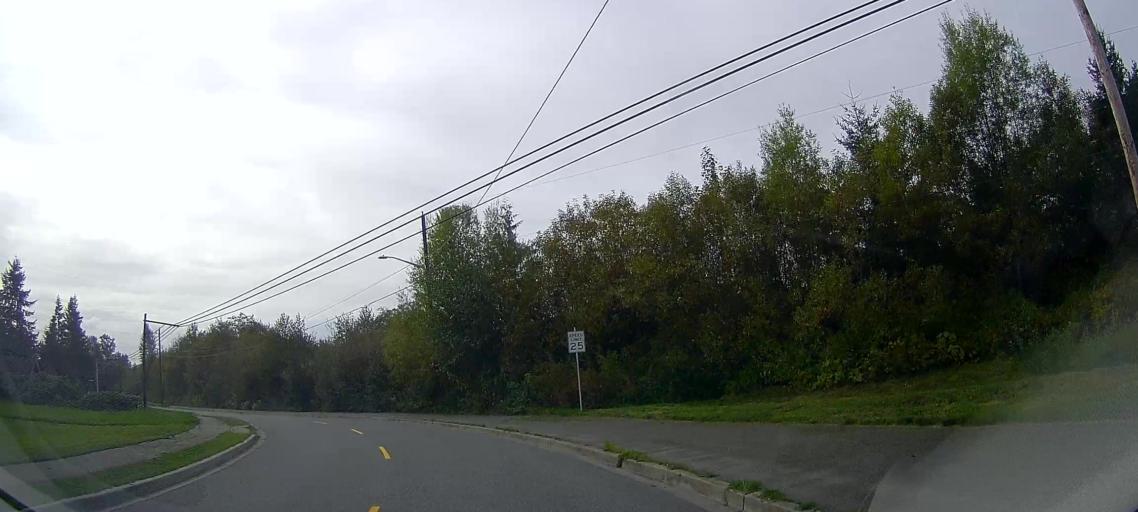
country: US
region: Washington
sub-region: Skagit County
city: Sedro-Woolley
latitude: 48.5225
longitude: -122.2126
